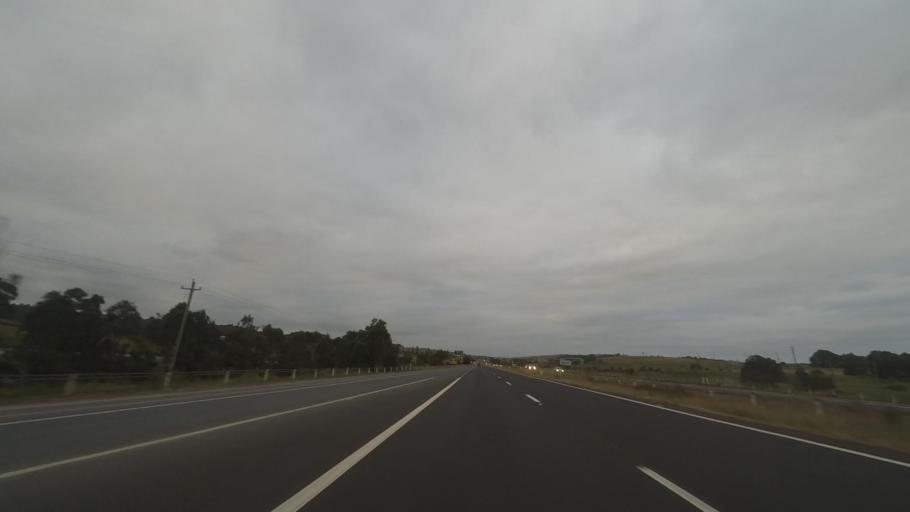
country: AU
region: New South Wales
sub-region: Shellharbour
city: Croom
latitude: -34.6041
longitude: 150.8396
